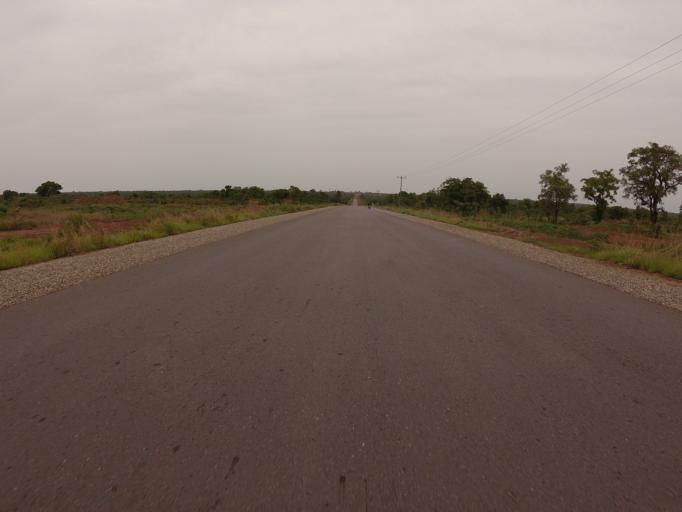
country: GH
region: Northern
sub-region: Yendi
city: Yendi
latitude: 9.2345
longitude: 0.0203
